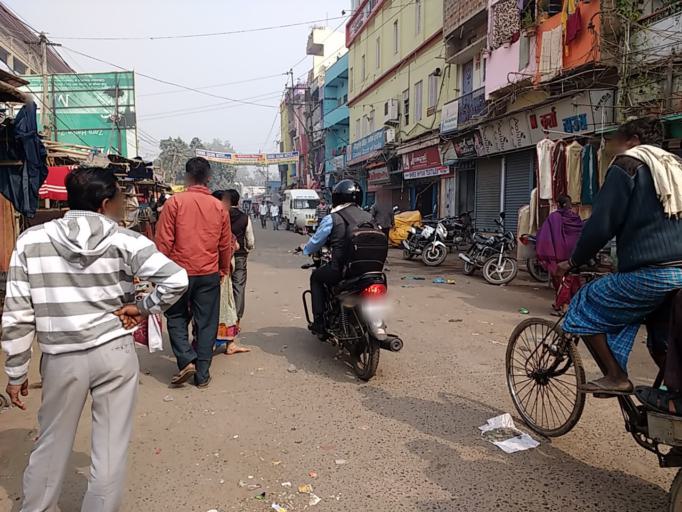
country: IN
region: Bihar
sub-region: Patna
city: Patna
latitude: 25.6150
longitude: 85.1539
